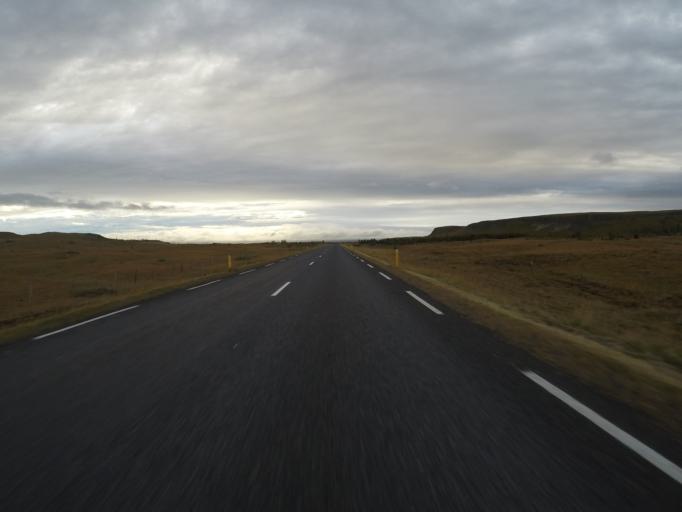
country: IS
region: South
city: Vestmannaeyjar
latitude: 64.0423
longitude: -20.1921
